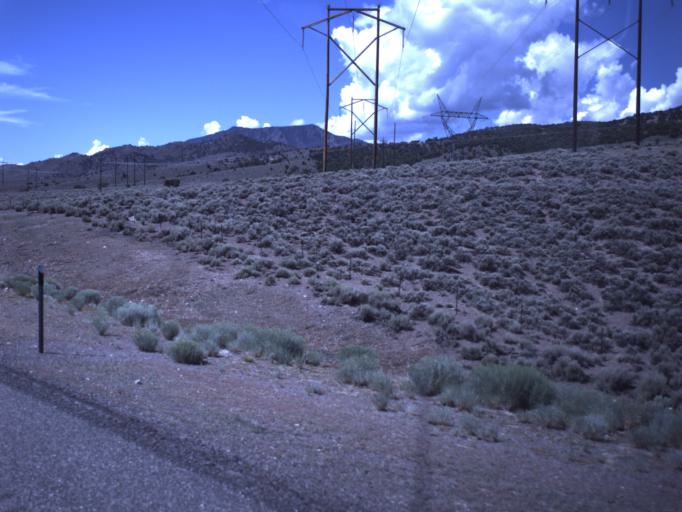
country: US
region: Utah
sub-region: Piute County
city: Junction
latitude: 38.3292
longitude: -112.2183
